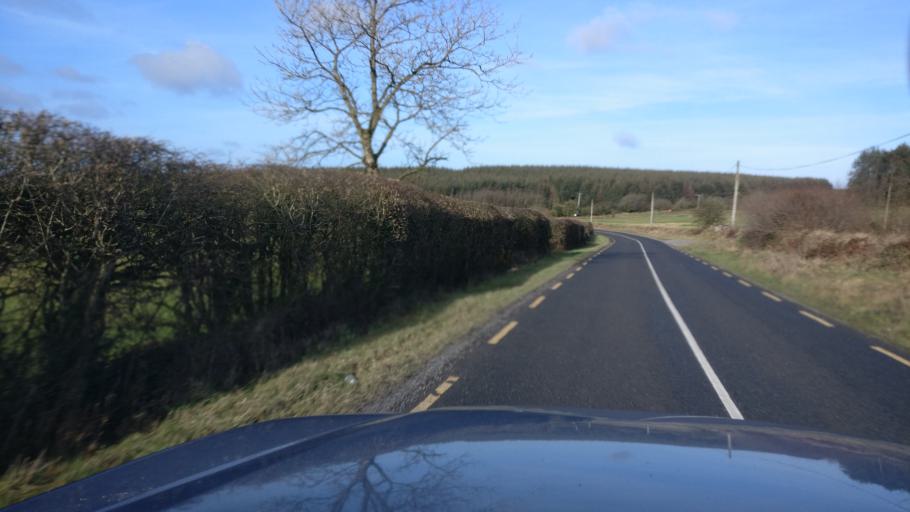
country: IE
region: Leinster
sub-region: Laois
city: Stradbally
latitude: 52.9185
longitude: -7.1877
